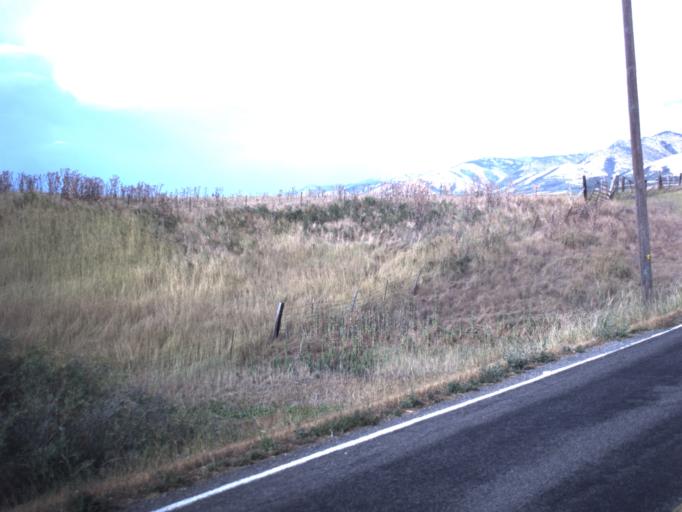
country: US
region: Utah
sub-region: Cache County
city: Lewiston
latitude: 41.9761
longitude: -111.8269
